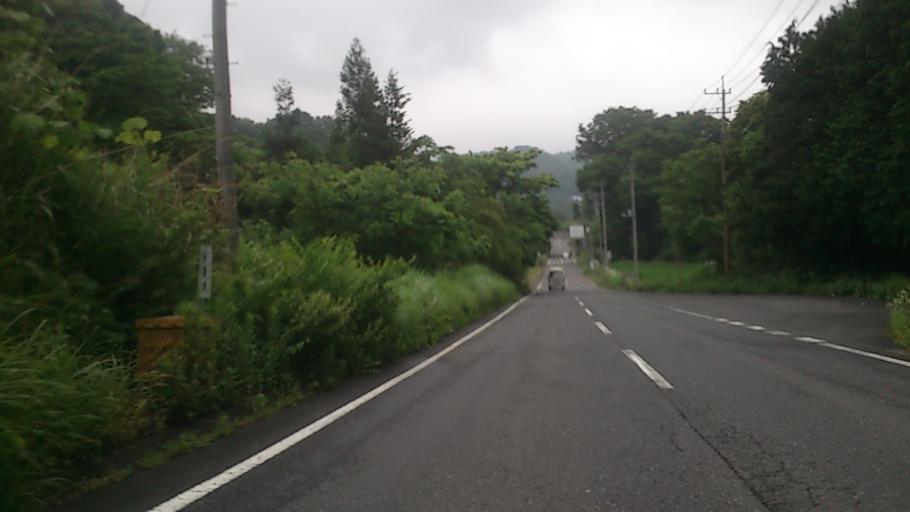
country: JP
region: Ibaraki
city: Omiya
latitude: 36.6313
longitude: 140.3916
